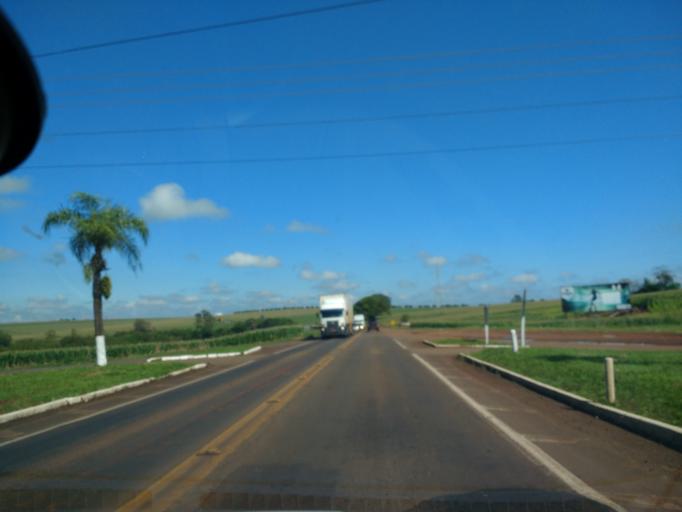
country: BR
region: Parana
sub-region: Terra Boa
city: Terra Boa
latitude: -23.6322
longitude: -52.4643
